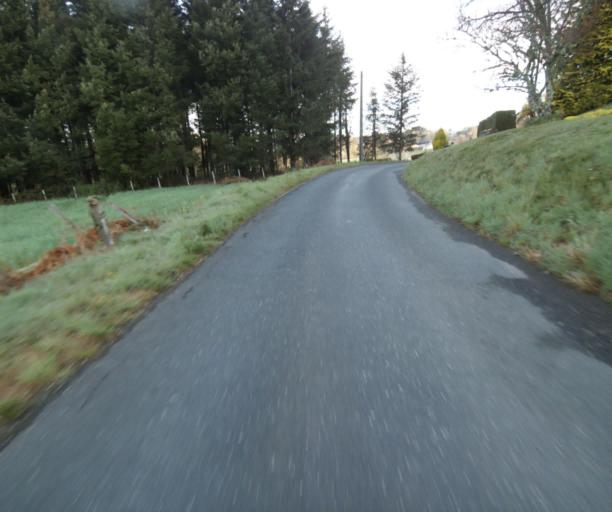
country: FR
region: Limousin
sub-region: Departement de la Correze
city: Correze
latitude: 45.3126
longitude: 1.8423
